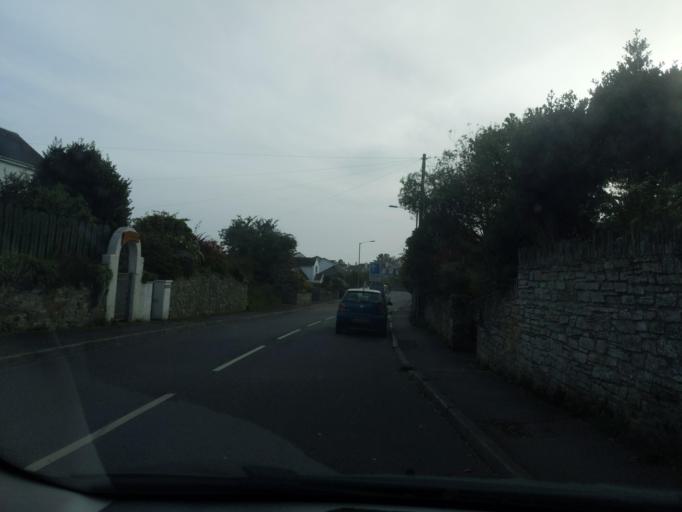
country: GB
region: England
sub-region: Cornwall
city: Looe
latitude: 50.3586
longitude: -4.4488
